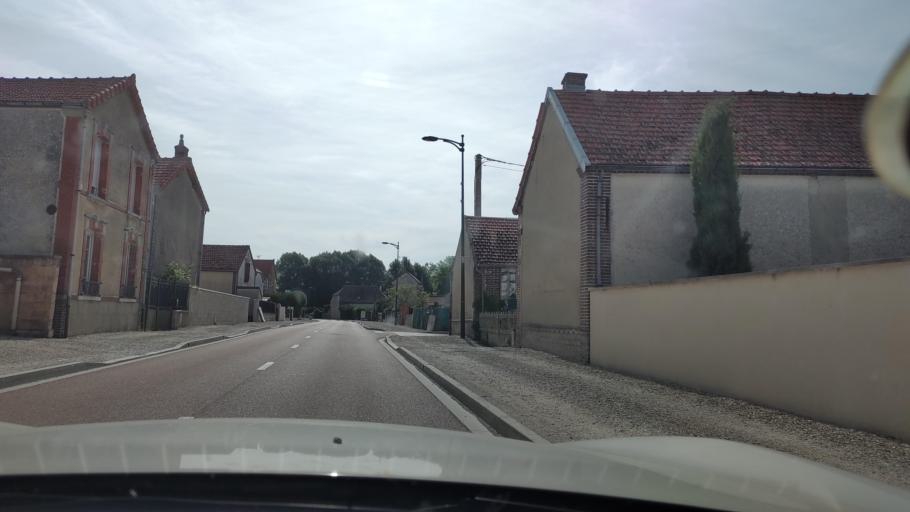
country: FR
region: Champagne-Ardenne
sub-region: Departement de l'Aube
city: Marigny-le-Chatel
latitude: 48.4019
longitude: 3.7433
